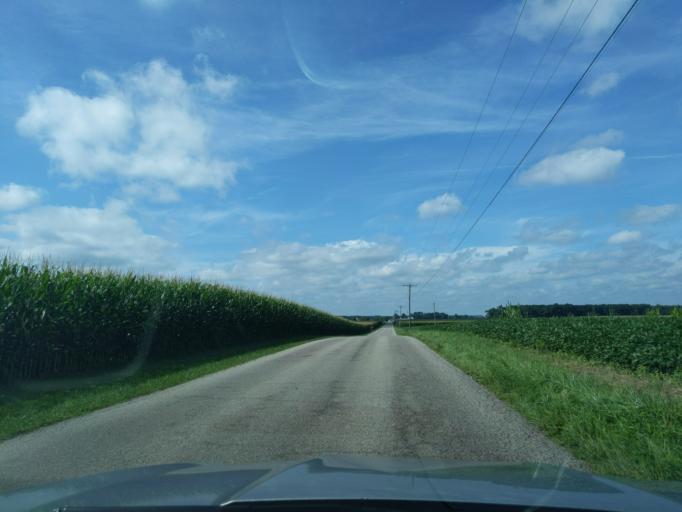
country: US
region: Indiana
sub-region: Ripley County
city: Batesville
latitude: 39.2860
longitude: -85.3477
